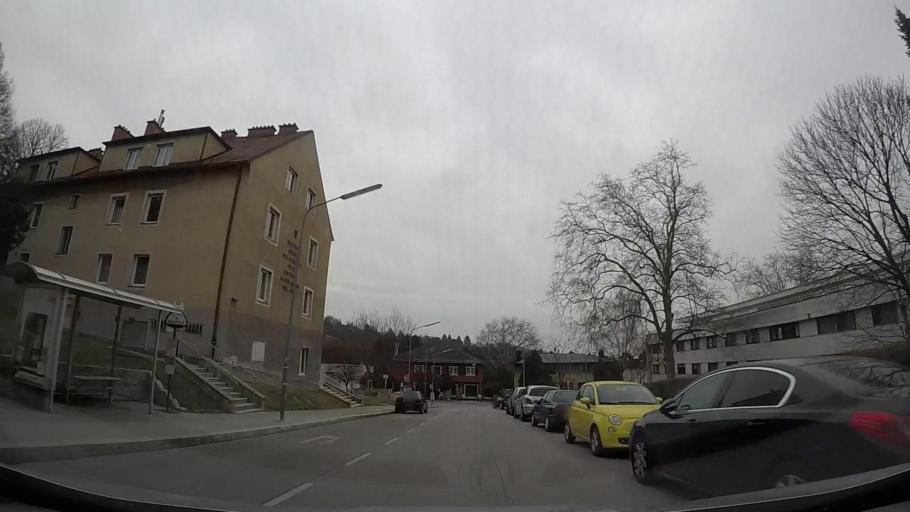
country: AT
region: Lower Austria
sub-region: Politischer Bezirk Wien-Umgebung
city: Purkersdorf
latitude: 48.2074
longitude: 16.2520
